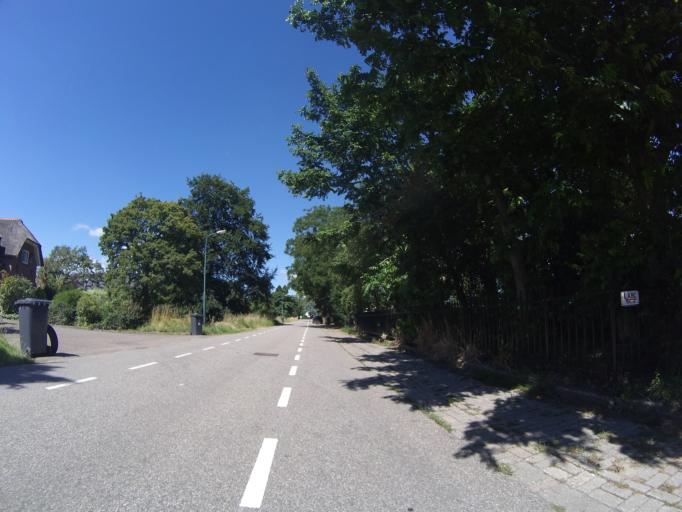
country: NL
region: Utrecht
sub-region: Stichtse Vecht
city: Maarssen
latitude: 52.0919
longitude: 5.0347
